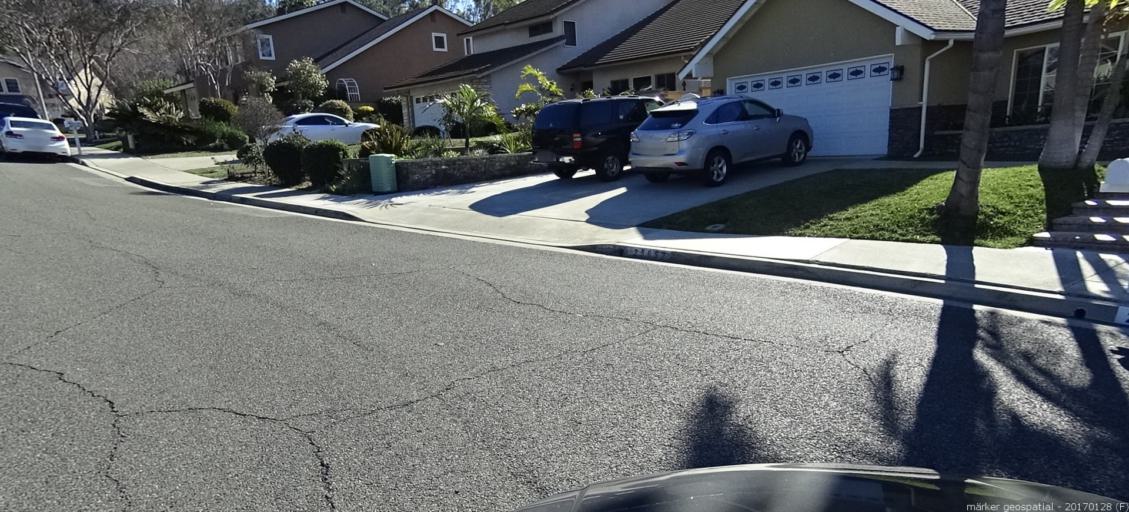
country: US
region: California
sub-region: Orange County
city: Lake Forest
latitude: 33.6513
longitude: -117.6828
